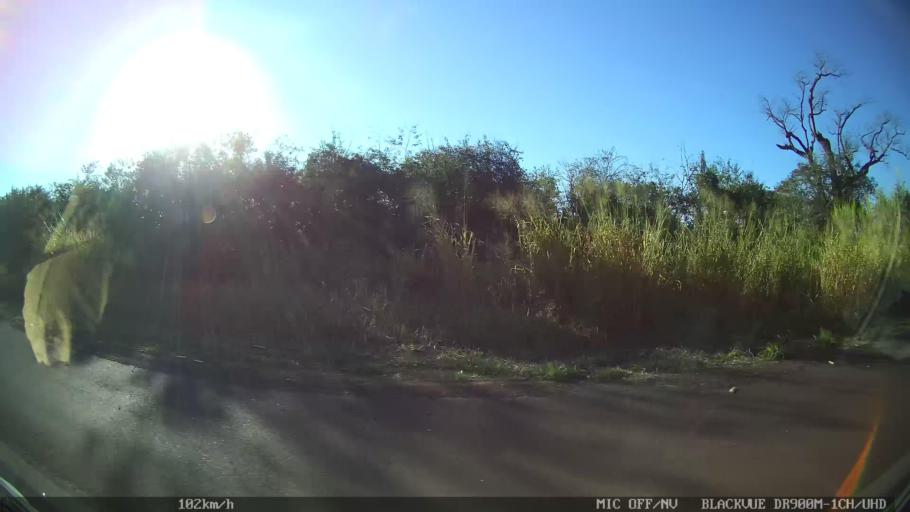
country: BR
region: Sao Paulo
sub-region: Guapiacu
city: Guapiacu
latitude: -20.7559
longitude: -49.1571
